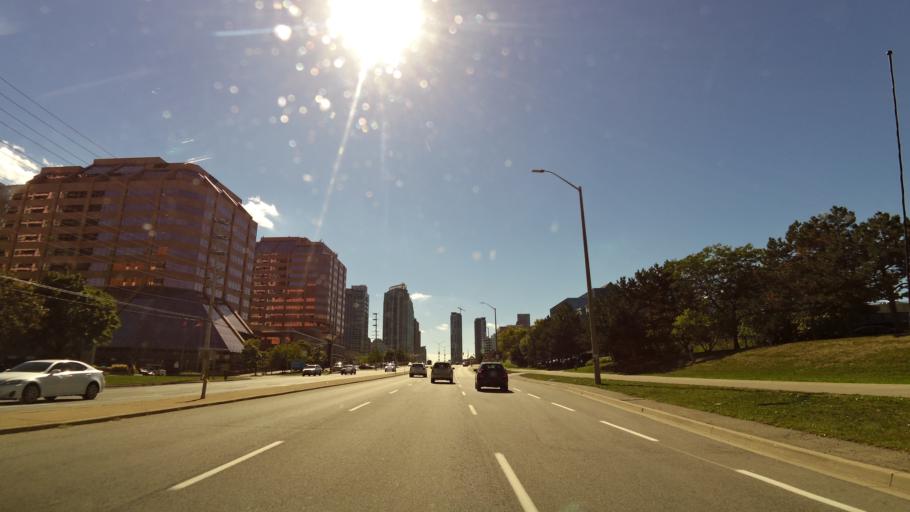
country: CA
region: Ontario
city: Mississauga
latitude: 43.5932
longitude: -79.6357
